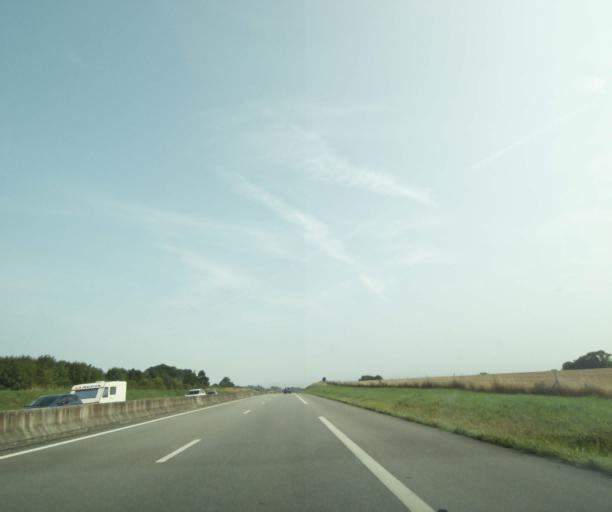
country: FR
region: Lower Normandy
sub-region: Departement de l'Orne
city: Radon
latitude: 48.5039
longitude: 0.1292
